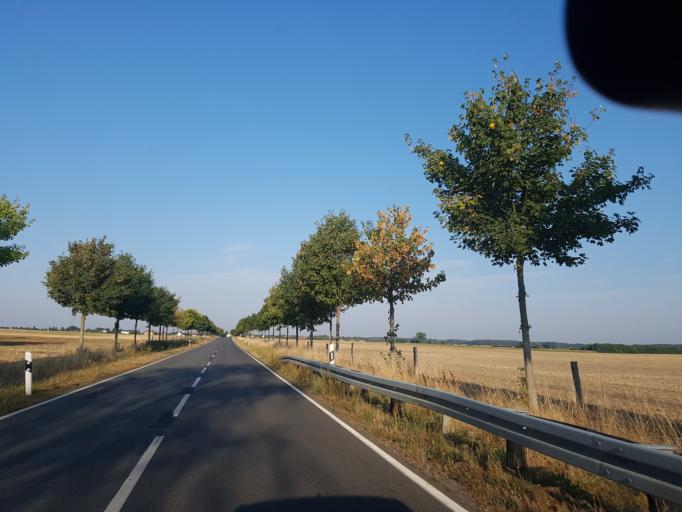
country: DE
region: Brandenburg
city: Plessa
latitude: 51.5355
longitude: 13.6501
